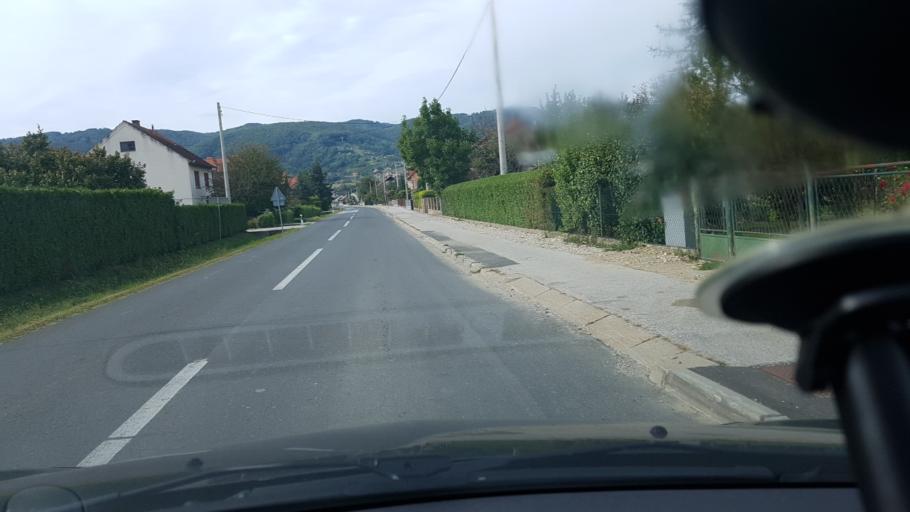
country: HR
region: Varazdinska
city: Remetinec
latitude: 46.1634
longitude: 16.3269
